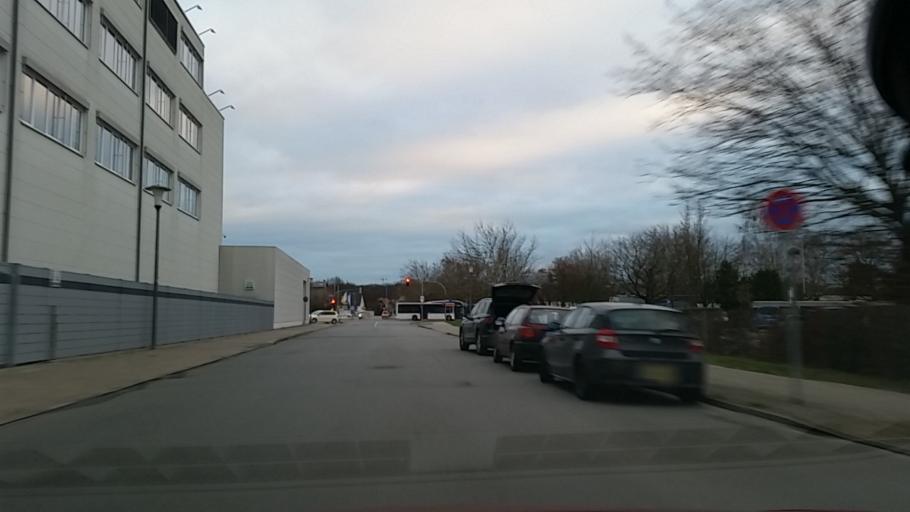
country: DE
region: Lower Saxony
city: Wolfsburg
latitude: 52.4283
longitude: 10.8099
